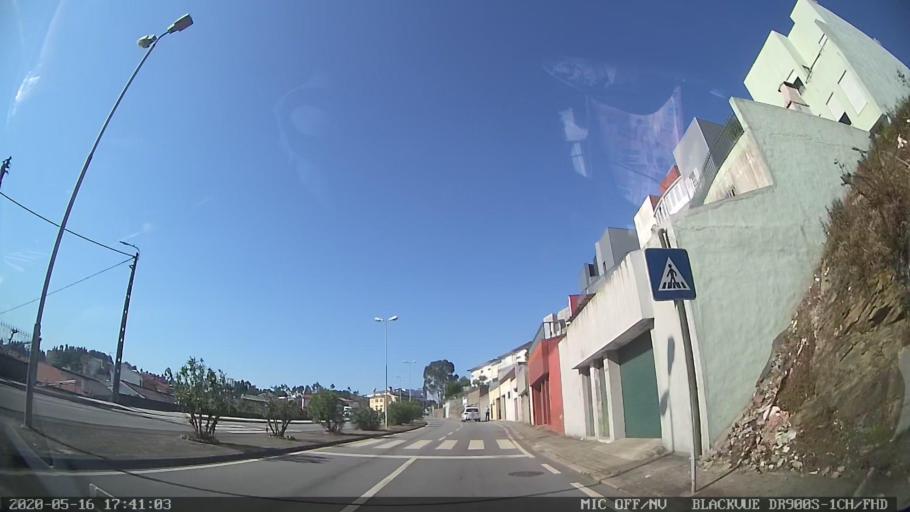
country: PT
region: Porto
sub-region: Valongo
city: Valongo
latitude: 41.1925
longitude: -8.5183
